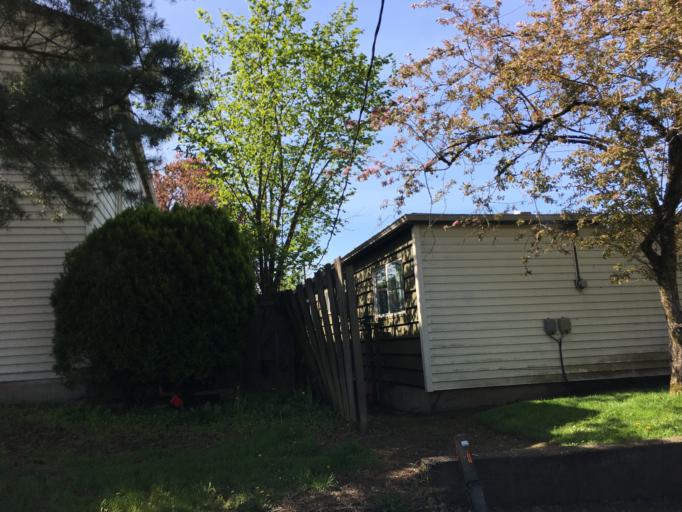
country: US
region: Oregon
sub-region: Multnomah County
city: Lents
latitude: 45.5285
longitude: -122.5692
